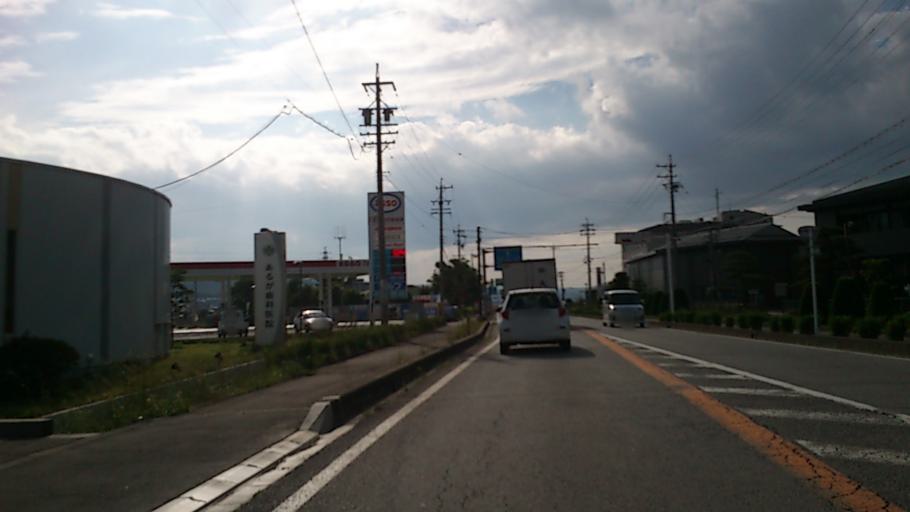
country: JP
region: Nagano
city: Saku
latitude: 36.2305
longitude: 138.4614
